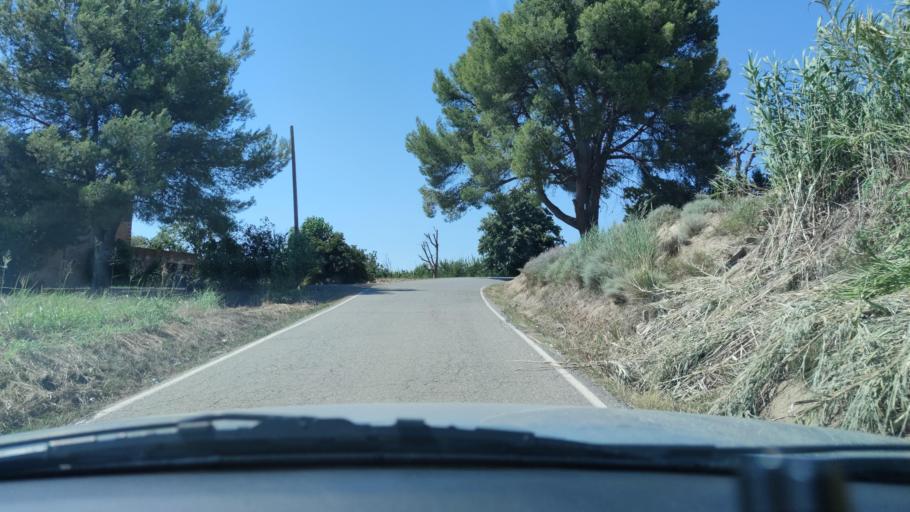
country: ES
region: Catalonia
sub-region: Provincia de Lleida
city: Torrefarrera
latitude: 41.6538
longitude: 0.6218
